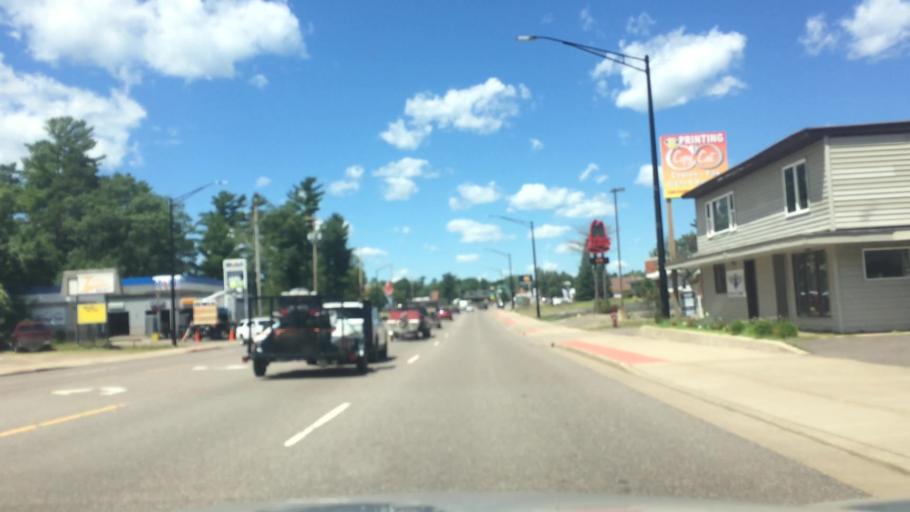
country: US
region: Wisconsin
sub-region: Vilas County
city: Lac du Flambeau
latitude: 45.8819
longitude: -89.7033
